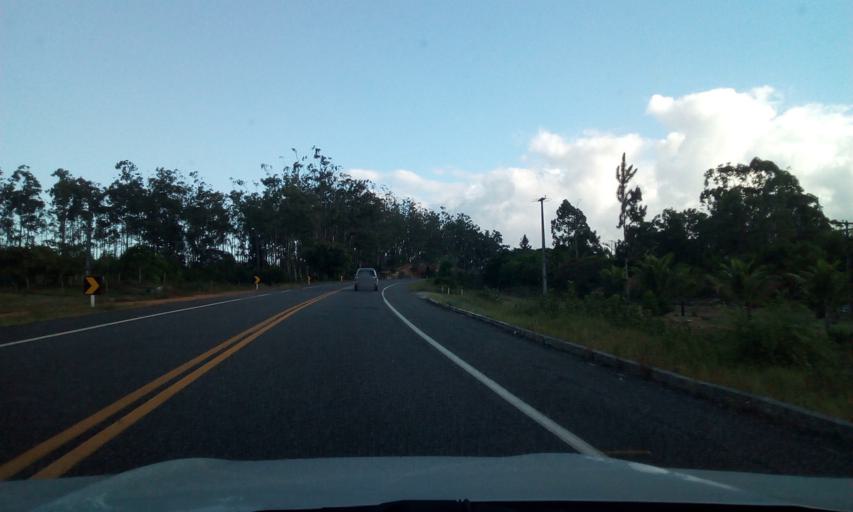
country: BR
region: Bahia
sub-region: Entre Rios
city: Entre Rios
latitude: -12.3088
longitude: -37.9044
